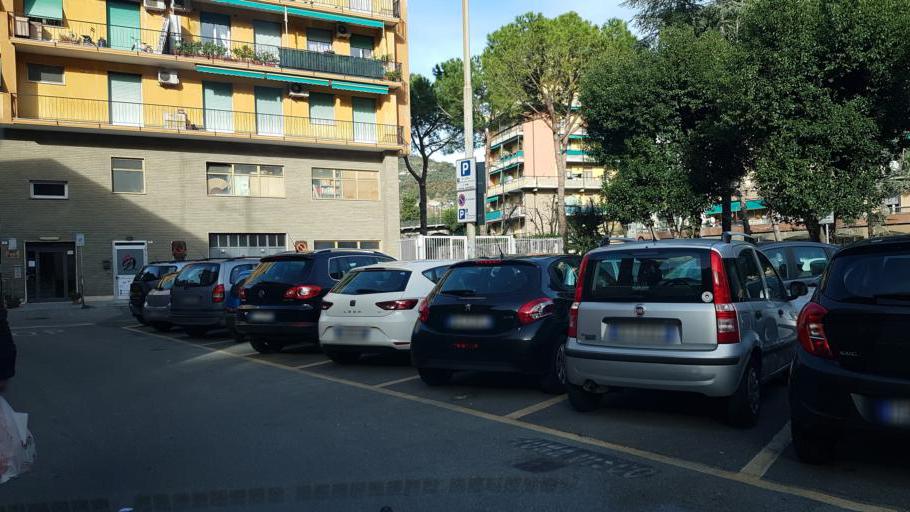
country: IT
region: Liguria
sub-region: Provincia di Genova
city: Recco
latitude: 44.3598
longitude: 9.1461
